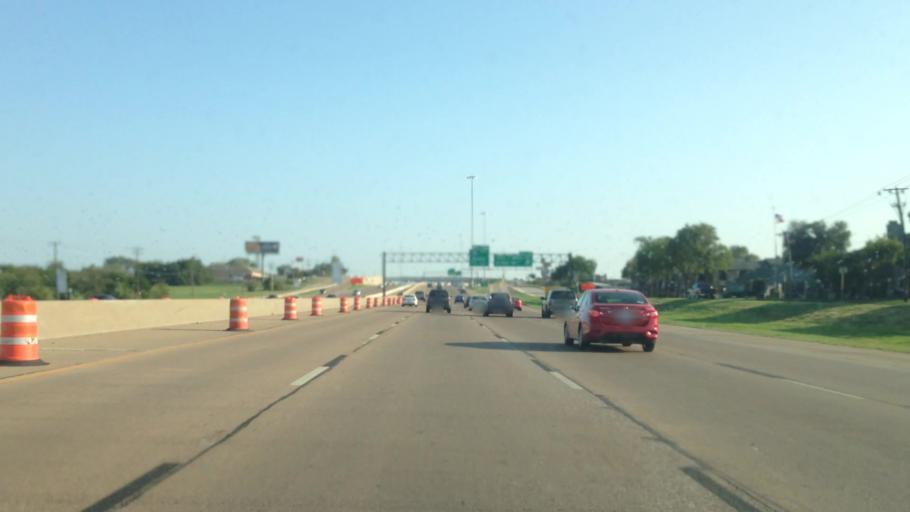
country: US
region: Texas
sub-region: Tarrant County
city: Richland Hills
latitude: 32.7734
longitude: -97.2128
